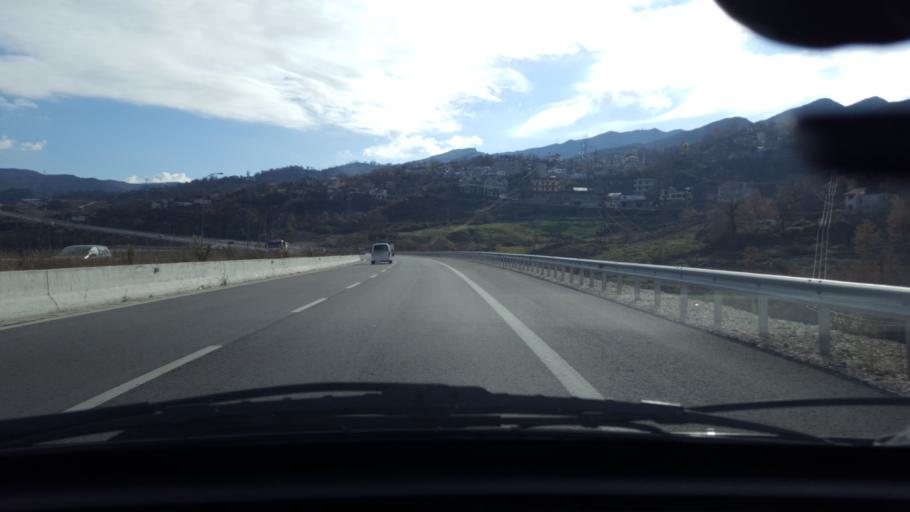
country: AL
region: Tirane
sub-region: Rrethi i Tiranes
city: Berzhite
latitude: 41.2299
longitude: 19.9296
